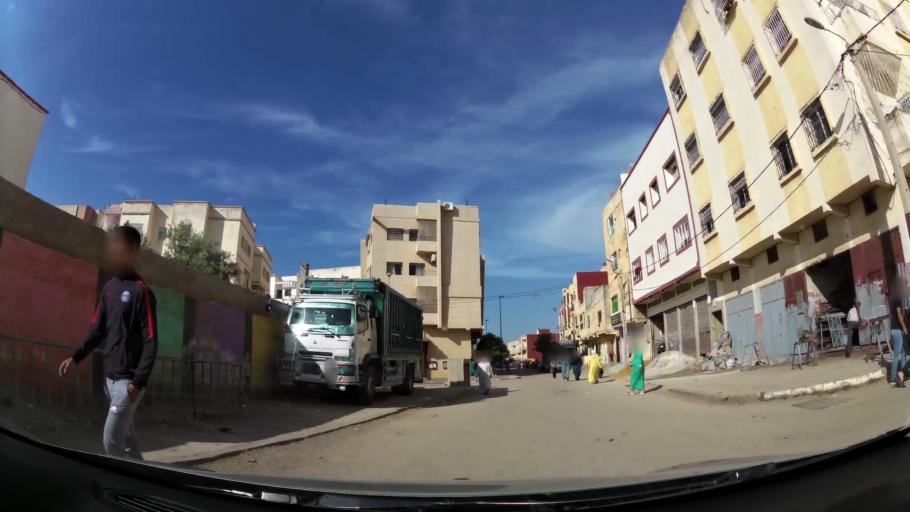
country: MA
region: Fes-Boulemane
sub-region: Fes
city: Fes
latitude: 34.0204
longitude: -5.0313
